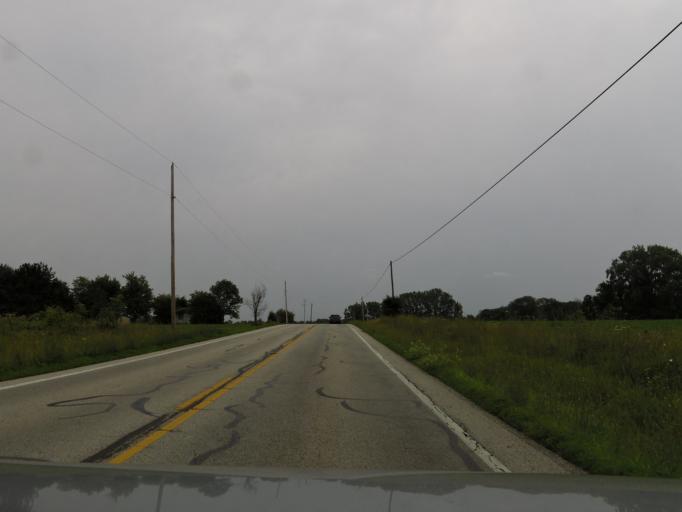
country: US
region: Ohio
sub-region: Warren County
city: Waynesville
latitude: 39.4944
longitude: -83.9722
